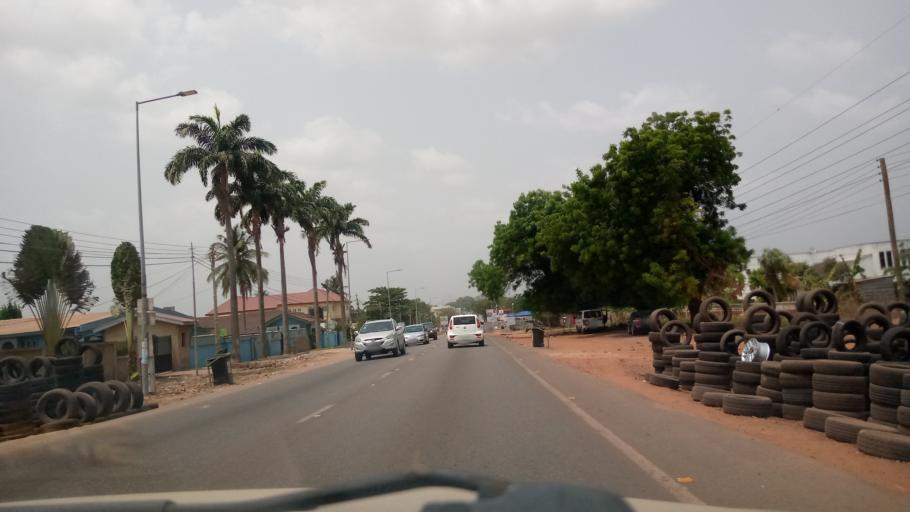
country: GH
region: Greater Accra
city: Dome
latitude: 5.6675
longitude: -0.2096
